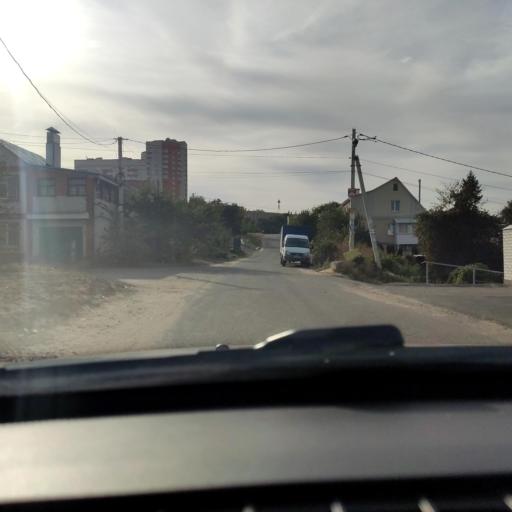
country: RU
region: Voronezj
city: Voronezh
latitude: 51.6425
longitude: 39.1897
